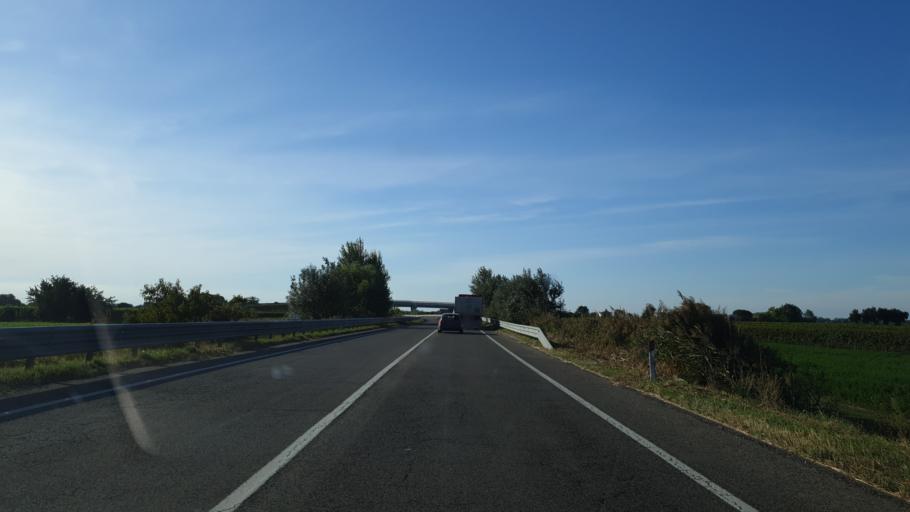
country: IT
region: Emilia-Romagna
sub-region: Provincia di Ravenna
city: Alfonsine
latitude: 44.5295
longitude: 12.0391
